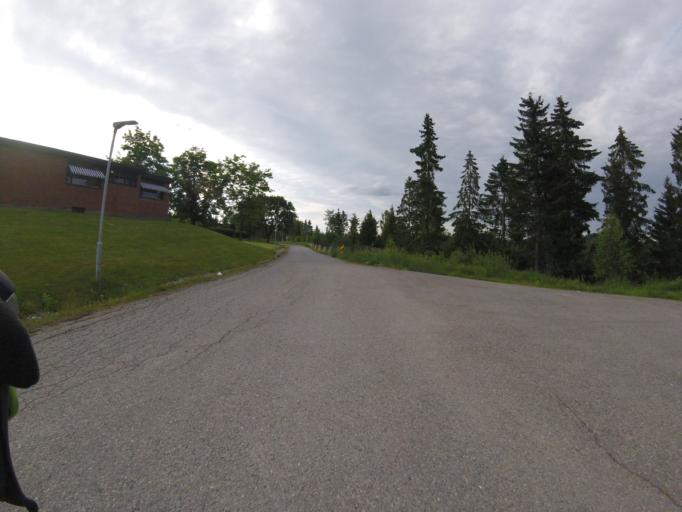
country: NO
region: Akershus
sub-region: Skedsmo
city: Lillestrom
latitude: 59.9716
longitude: 11.0121
